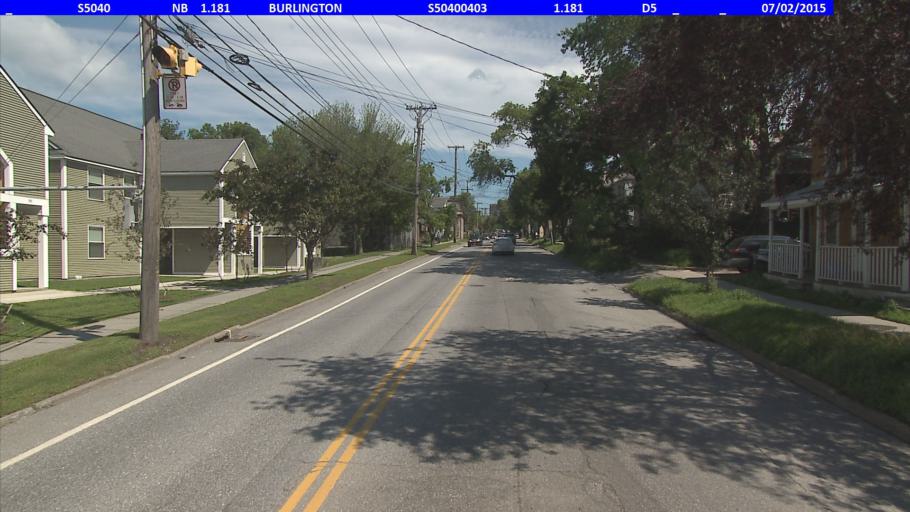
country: US
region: Vermont
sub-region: Chittenden County
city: Burlington
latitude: 44.4724
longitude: -73.2153
